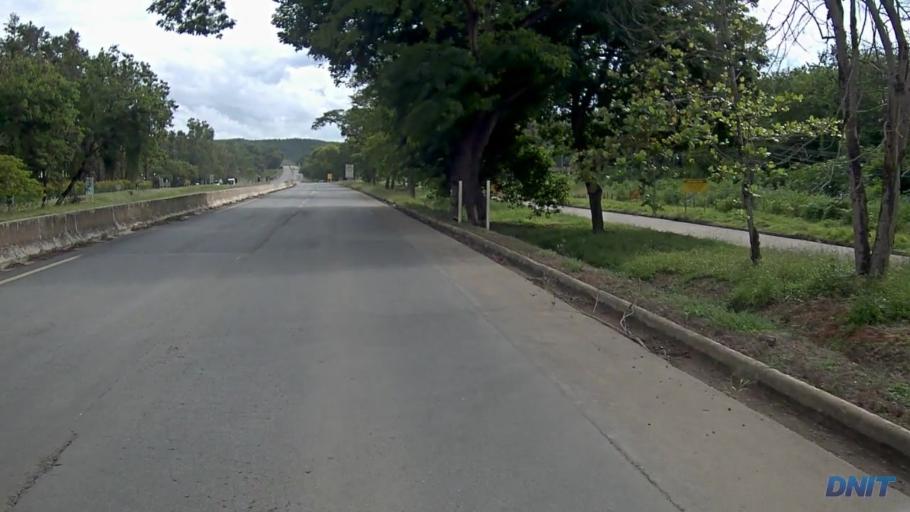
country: BR
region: Minas Gerais
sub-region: Ipaba
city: Ipaba
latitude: -19.3124
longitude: -42.3959
